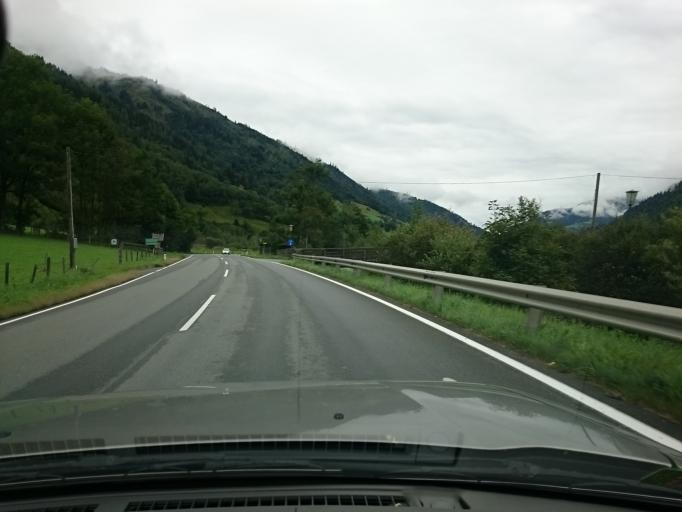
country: AT
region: Salzburg
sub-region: Politischer Bezirk Zell am See
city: Bruck an der Grossglocknerstrasse
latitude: 47.2360
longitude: 12.8263
